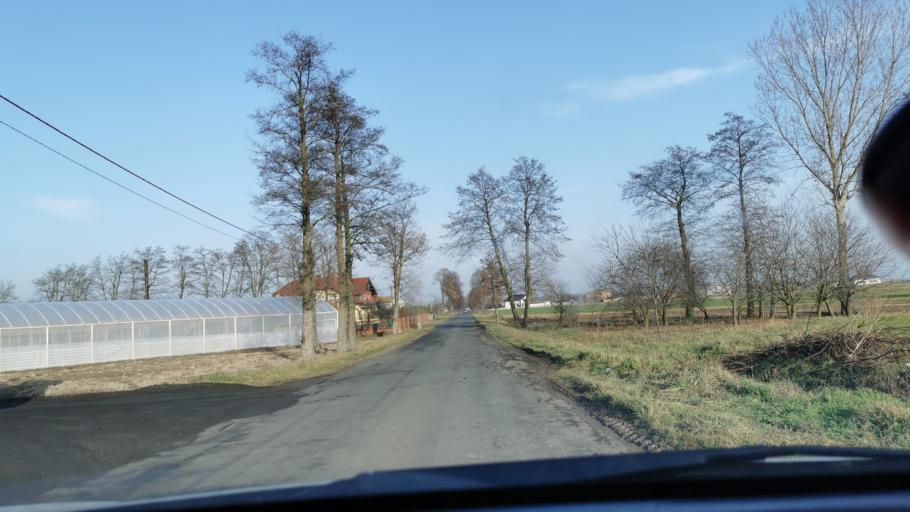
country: PL
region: Greater Poland Voivodeship
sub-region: Powiat kaliski
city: Opatowek
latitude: 51.6788
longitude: 18.3037
